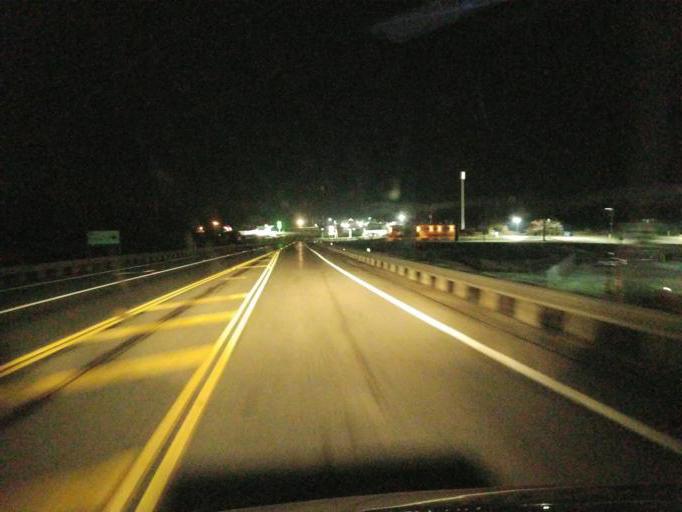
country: US
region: Ohio
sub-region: Morrow County
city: Mount Gilead
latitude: 40.4962
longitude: -82.7166
